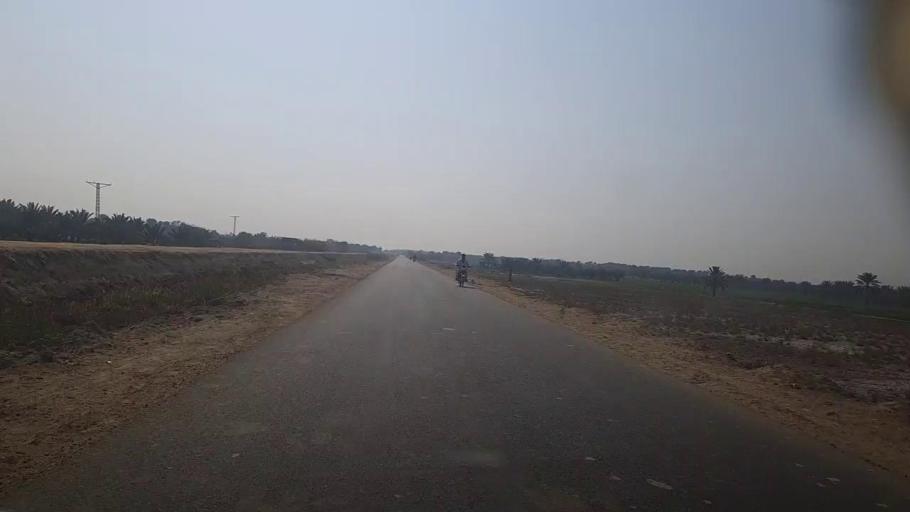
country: PK
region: Sindh
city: Khairpur
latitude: 27.4736
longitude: 68.8227
